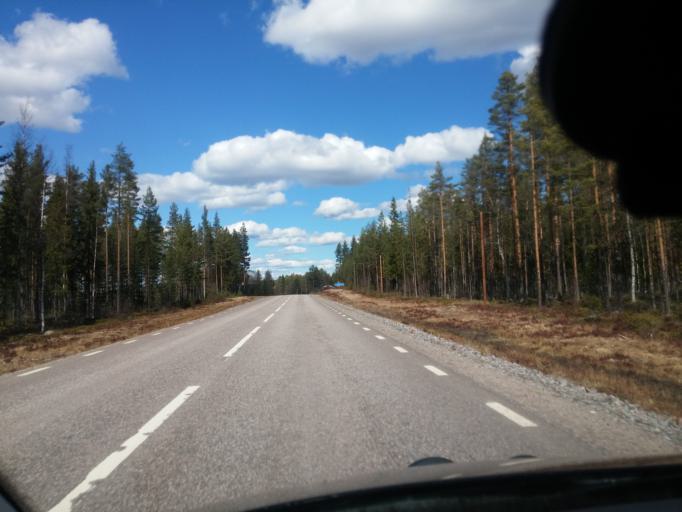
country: SE
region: Gaevleborg
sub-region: Ovanakers Kommun
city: Edsbyn
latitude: 61.2663
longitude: 15.8902
